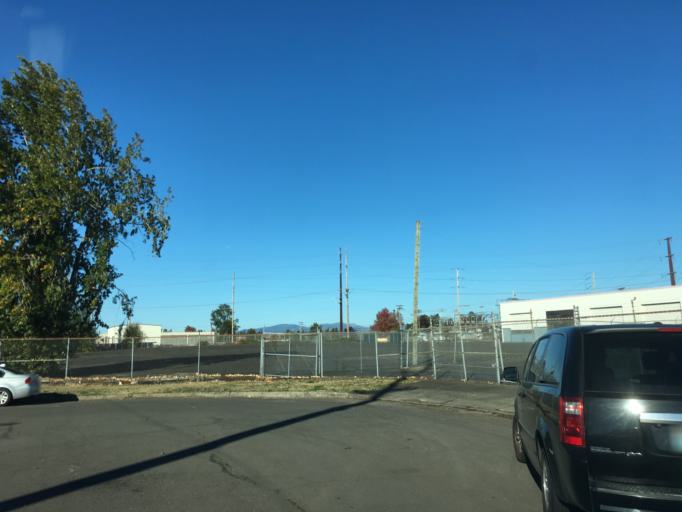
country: US
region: Oregon
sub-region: Multnomah County
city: Gresham
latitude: 45.4996
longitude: -122.4160
